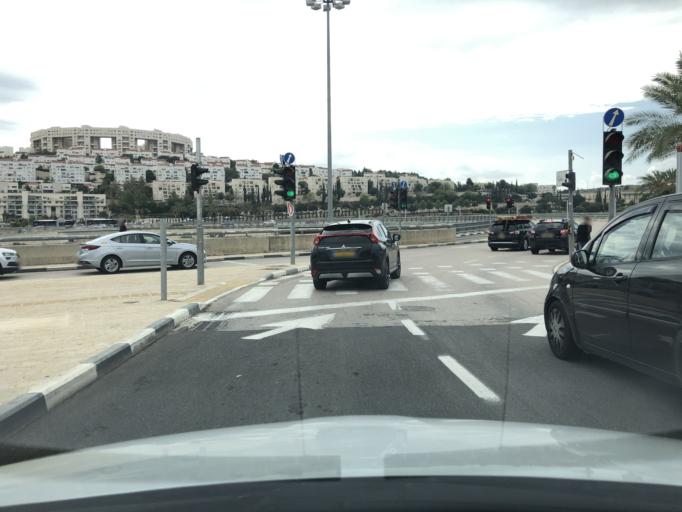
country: IL
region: Central District
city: Modiin
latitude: 31.9006
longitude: 35.0052
